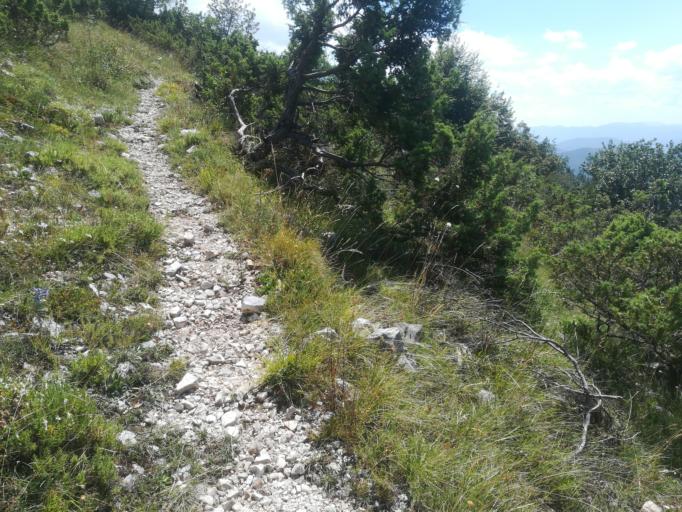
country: IT
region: Umbria
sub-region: Provincia di Perugia
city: Scheggino
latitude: 42.6724
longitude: 12.8566
